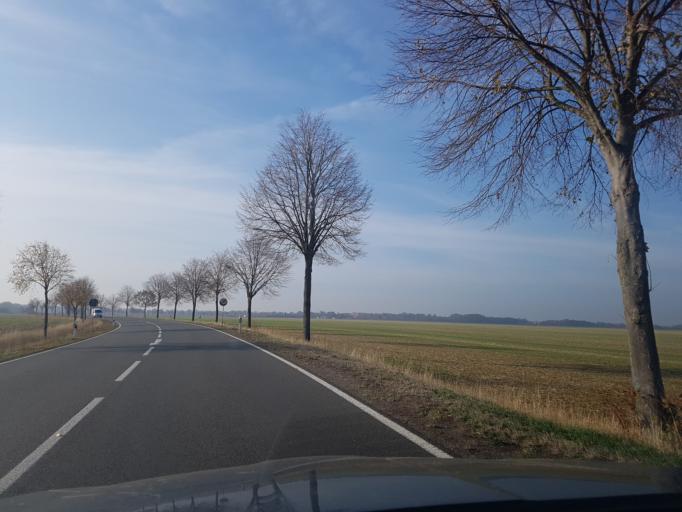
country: DE
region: Saxony
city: Beilrode
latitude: 51.5491
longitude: 13.0832
